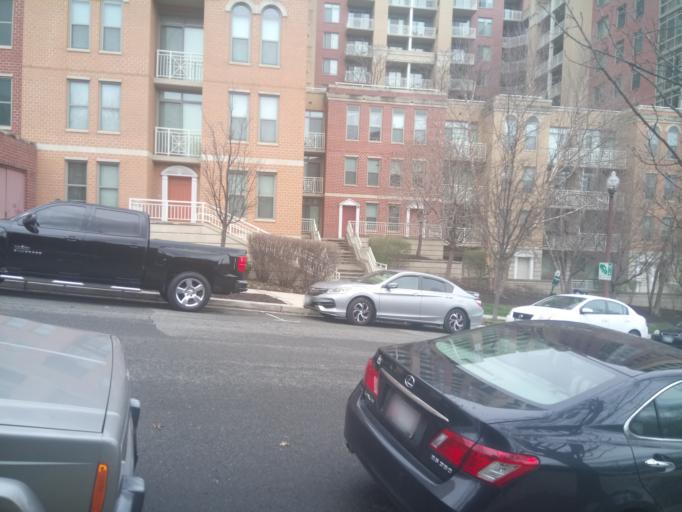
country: US
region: Virginia
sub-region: Arlington County
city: Arlington
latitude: 38.8884
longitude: -77.0825
